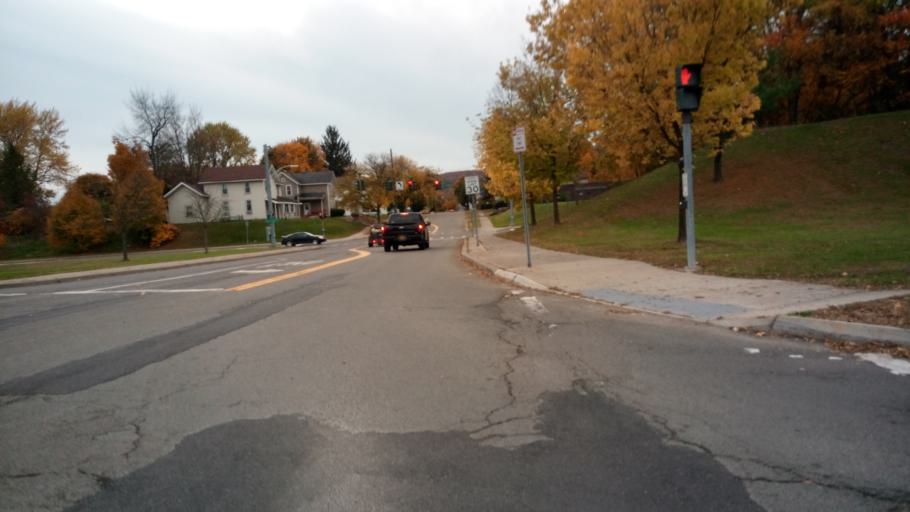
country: US
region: New York
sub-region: Chemung County
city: Elmira
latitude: 42.0746
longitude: -76.8002
